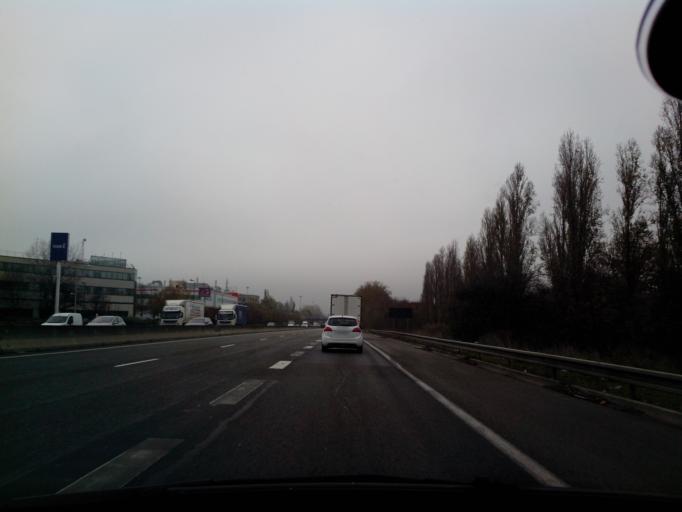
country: FR
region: Ile-de-France
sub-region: Departement de l'Essonne
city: Wissous
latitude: 48.7293
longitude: 2.3145
